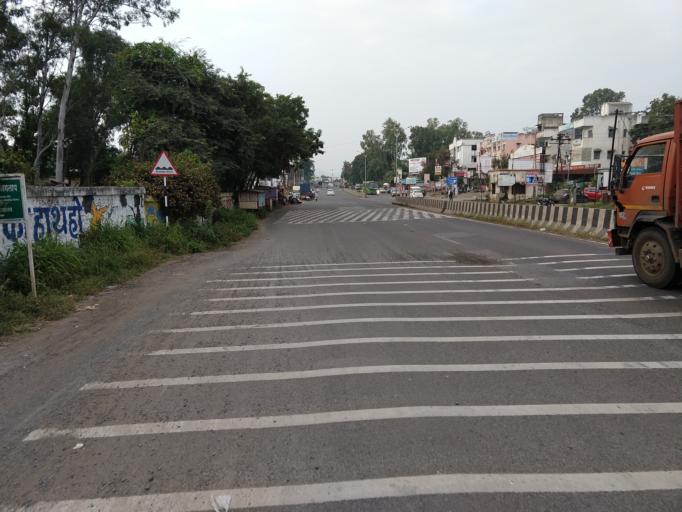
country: IN
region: Maharashtra
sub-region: Pune Division
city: Sasvad
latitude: 18.3511
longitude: 74.0288
